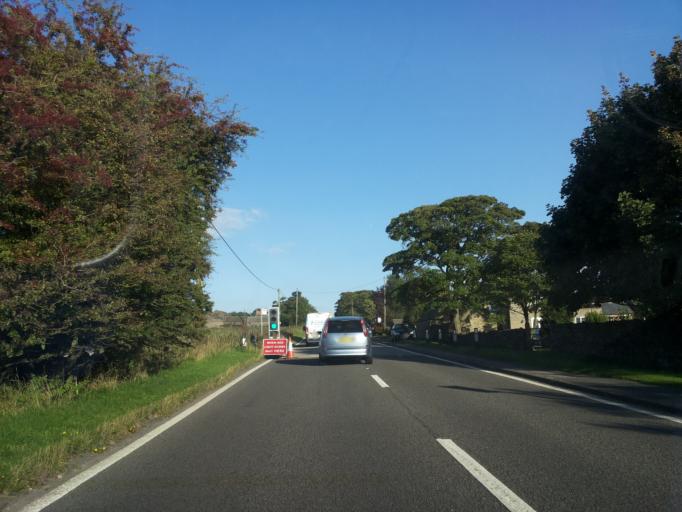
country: GB
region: England
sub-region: Derbyshire
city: Dronfield
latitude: 53.2381
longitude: -1.5478
